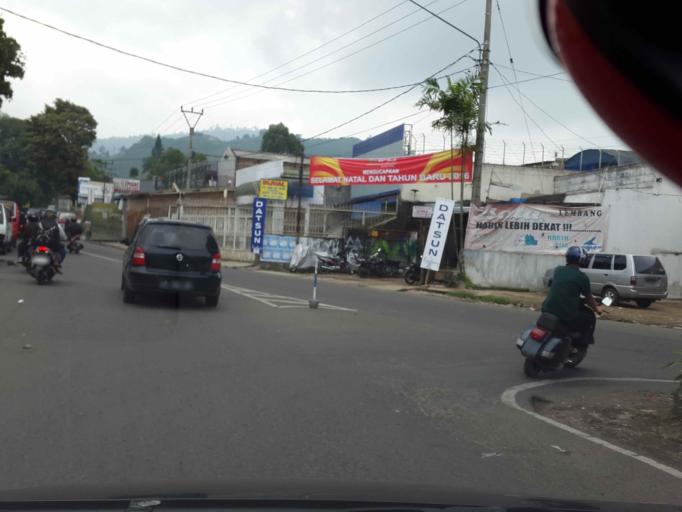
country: ID
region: West Java
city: Lembang
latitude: -6.8144
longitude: 107.6229
